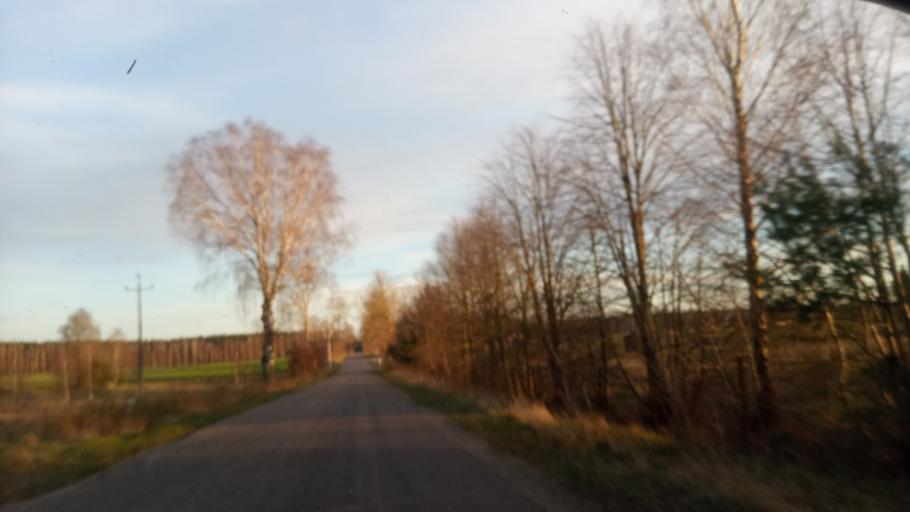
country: PL
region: West Pomeranian Voivodeship
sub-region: Powiat szczecinecki
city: Lubowo
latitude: 53.5824
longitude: 16.3937
